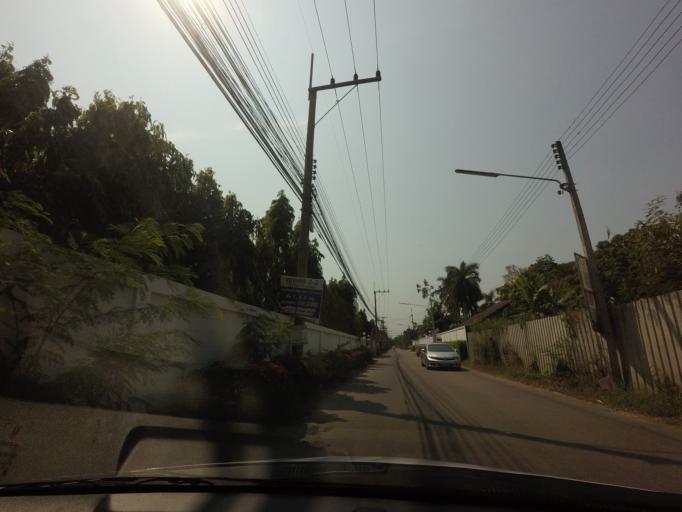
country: TH
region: Nakhon Pathom
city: Sam Phran
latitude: 13.7206
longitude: 100.2671
